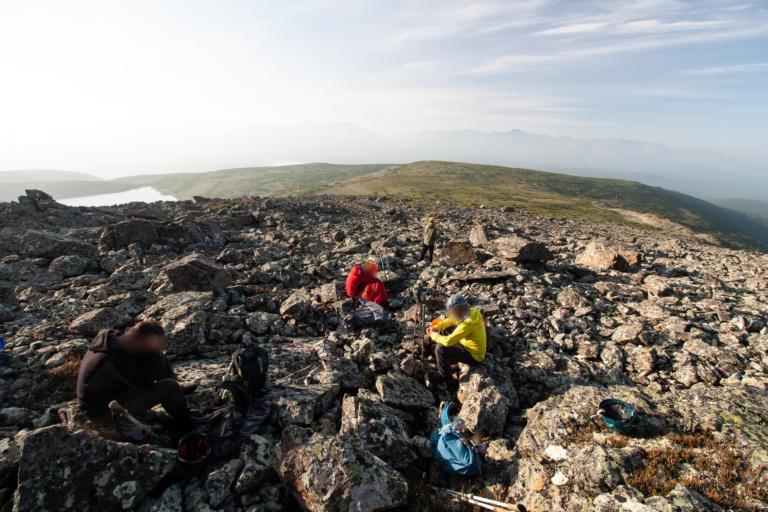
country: RU
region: Respublika Buryatiya
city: Kichera
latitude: 56.3588
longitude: 110.0827
